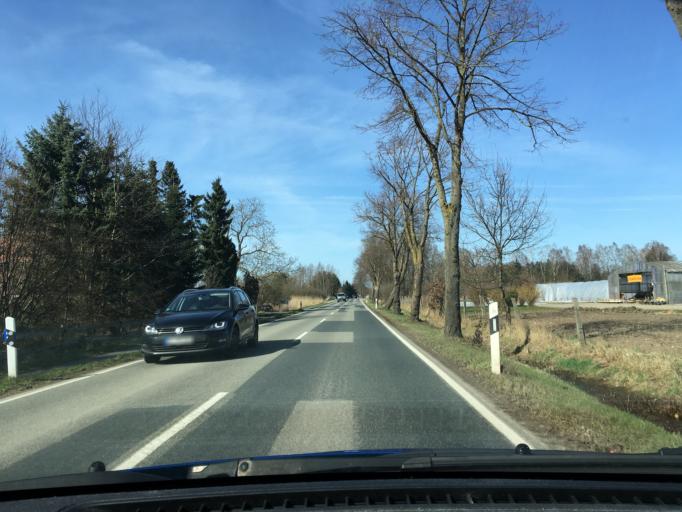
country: DE
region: Lower Saxony
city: Winsen
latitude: 53.3799
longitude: 10.2453
